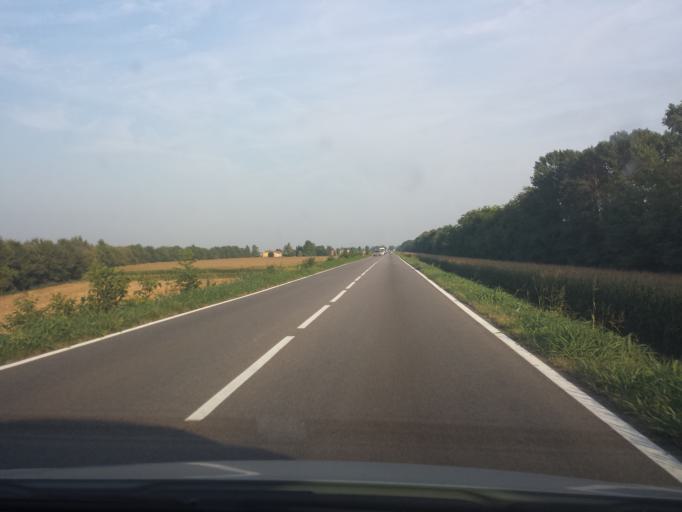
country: IT
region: Veneto
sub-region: Provincia di Venezia
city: Passarella
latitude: 45.6052
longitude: 12.6000
